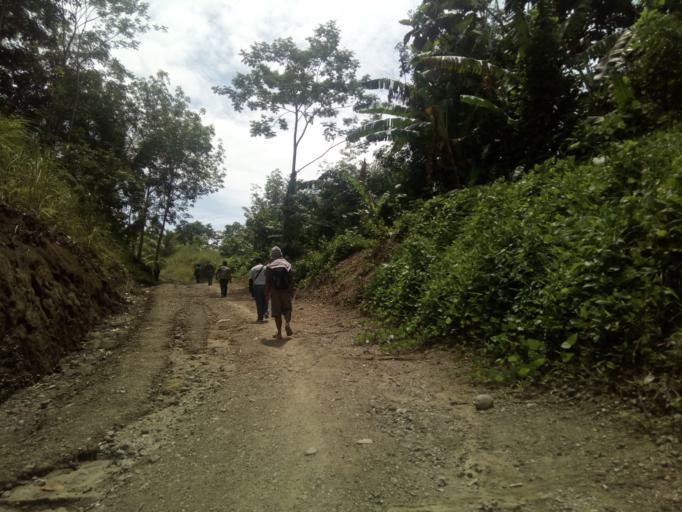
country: PH
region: Caraga
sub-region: Province of Agusan del Sur
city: Santa Josefa
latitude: 7.9438
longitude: 125.9836
